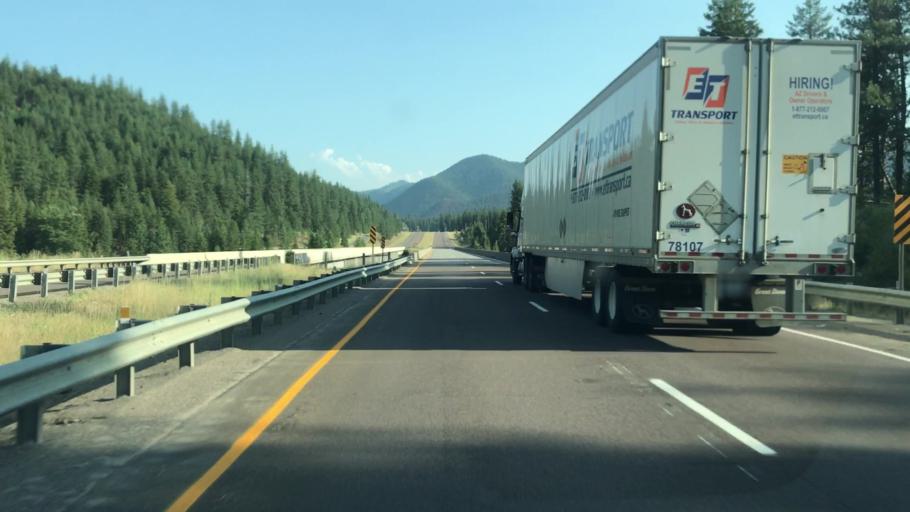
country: US
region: Montana
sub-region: Mineral County
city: Superior
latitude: 47.0701
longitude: -114.7650
